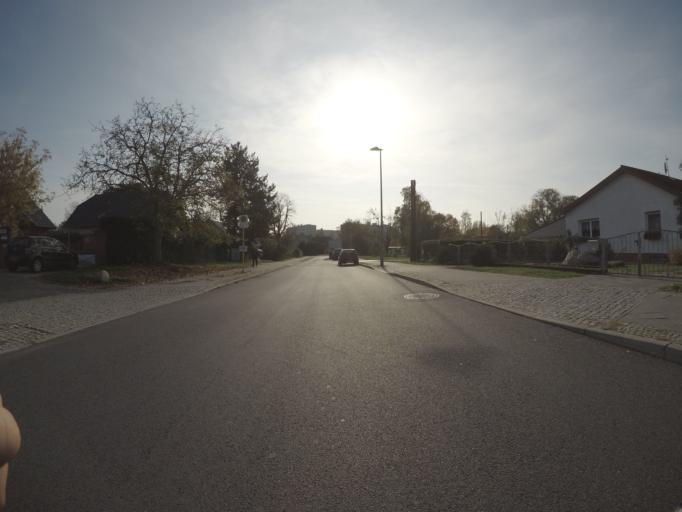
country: DE
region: Berlin
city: Altglienicke
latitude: 52.4007
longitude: 13.5382
